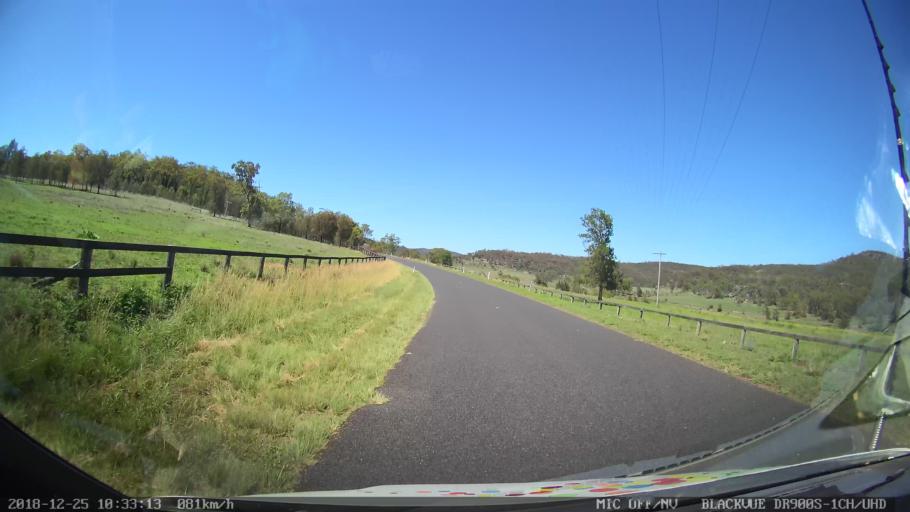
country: AU
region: New South Wales
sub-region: Upper Hunter Shire
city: Merriwa
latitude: -32.3801
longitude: 150.4084
